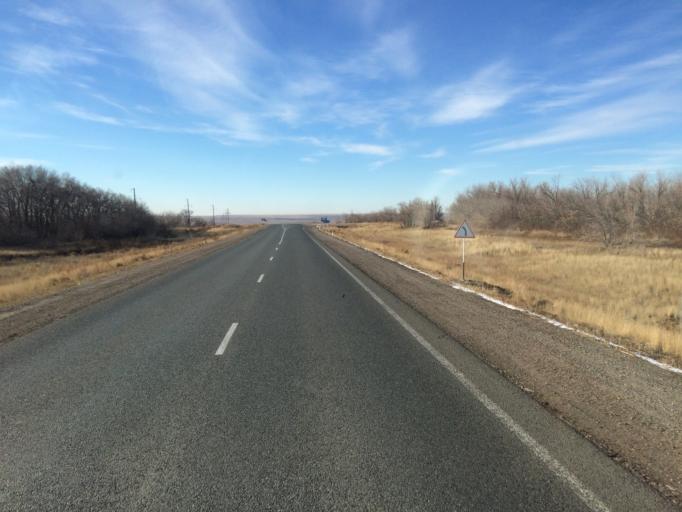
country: KZ
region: Aqtoebe
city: Aqtobe
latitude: 50.2476
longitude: 56.7923
